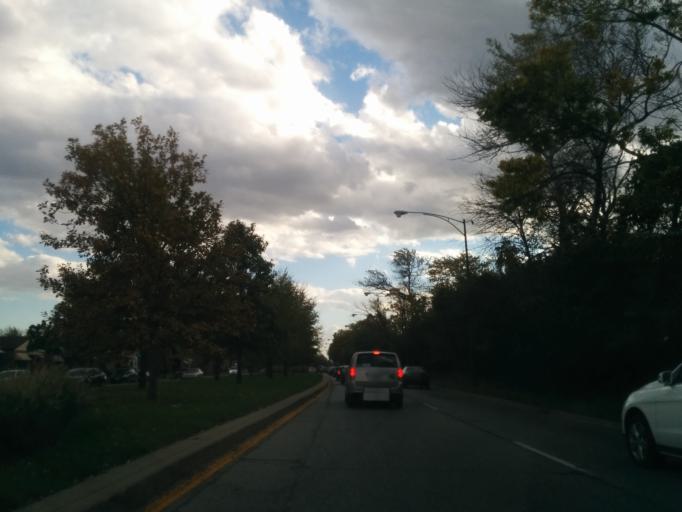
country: US
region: Illinois
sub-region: Cook County
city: Norridge
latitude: 41.9499
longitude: -87.8368
